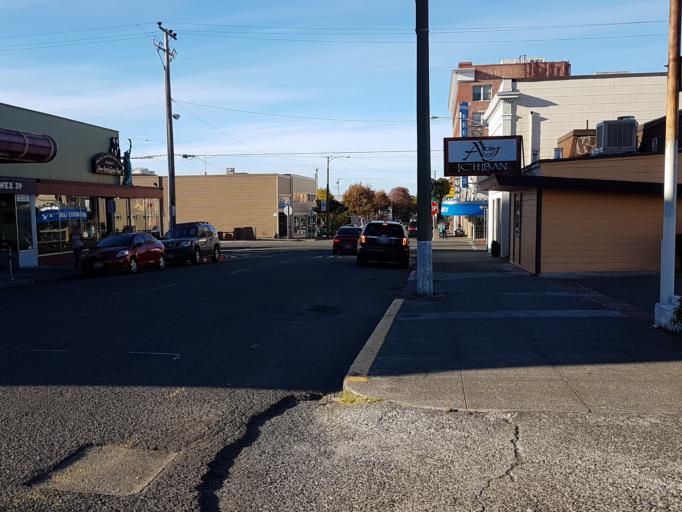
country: US
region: California
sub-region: Humboldt County
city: Eureka
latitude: 40.8006
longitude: -124.1656
